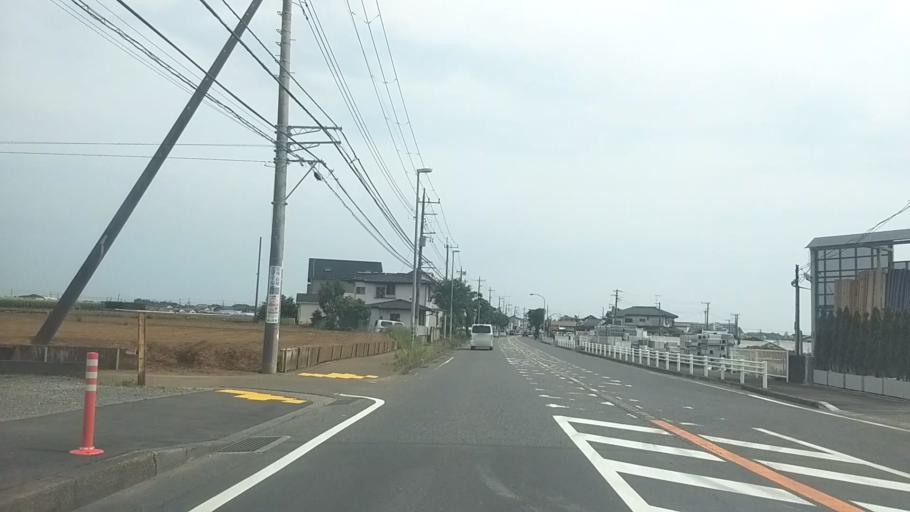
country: JP
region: Kanagawa
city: Fujisawa
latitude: 35.3745
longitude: 139.4780
